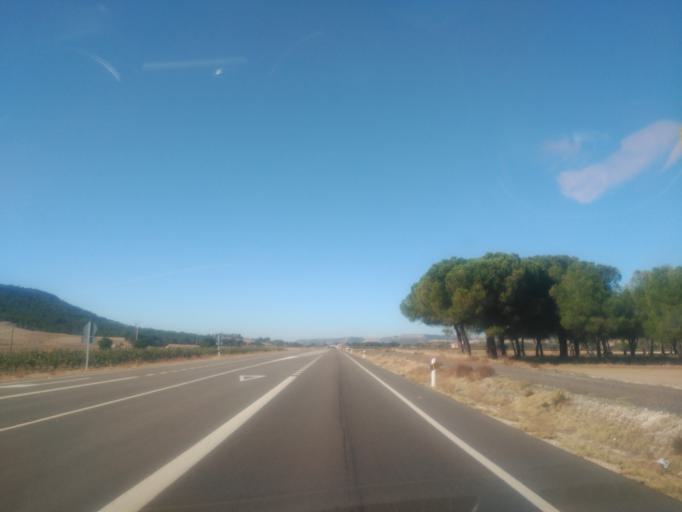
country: ES
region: Castille and Leon
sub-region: Provincia de Valladolid
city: Quintanilla de Onesimo
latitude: 41.6276
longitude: -4.3286
